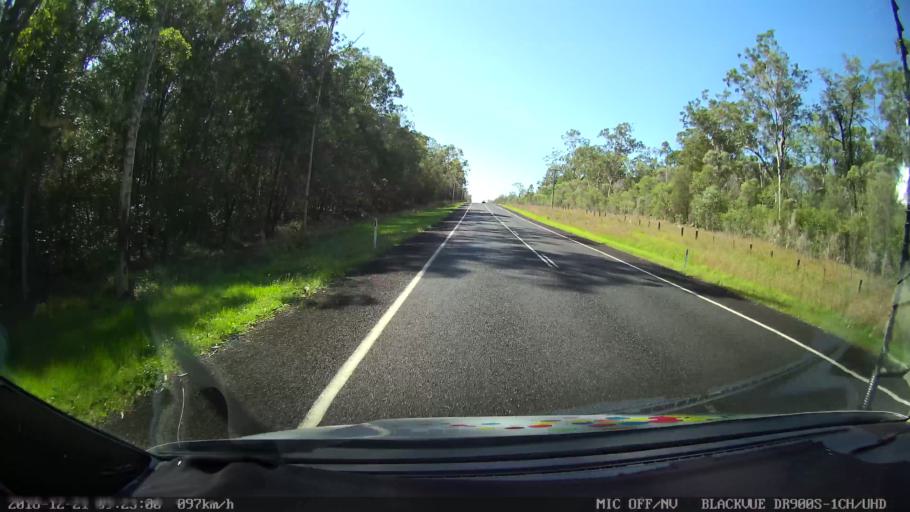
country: AU
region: New South Wales
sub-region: Clarence Valley
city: Maclean
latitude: -29.3491
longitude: 153.0098
